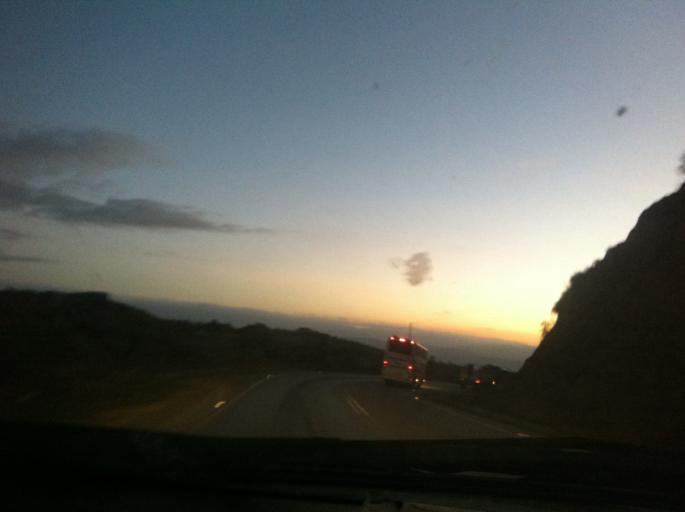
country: BO
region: Cochabamba
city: Irpa Irpa
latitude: -17.6704
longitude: -66.4395
